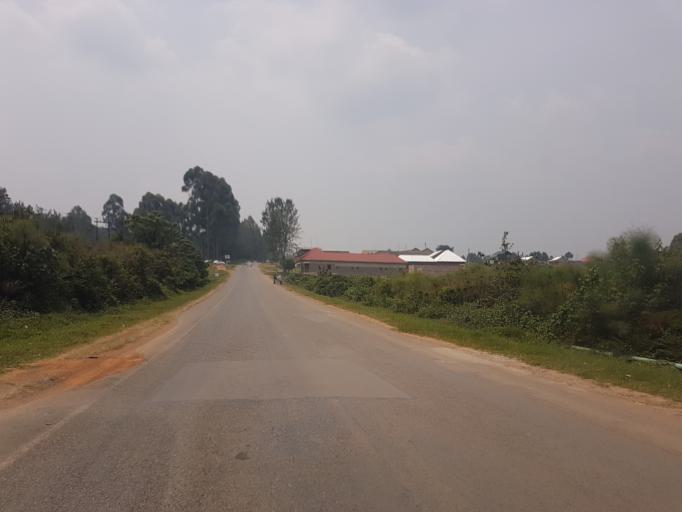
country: UG
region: Western Region
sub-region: Bushenyi District
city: Bushenyi
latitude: -0.5437
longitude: 30.2156
